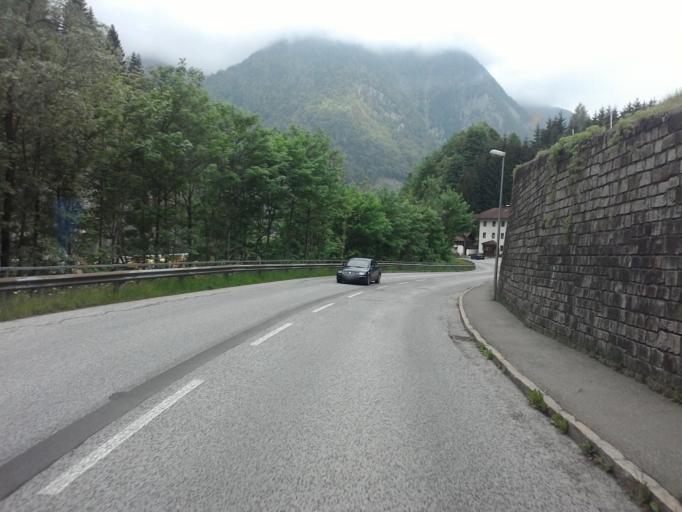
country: AT
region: Styria
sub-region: Politischer Bezirk Leoben
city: Hieflau
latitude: 47.6007
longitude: 14.7491
